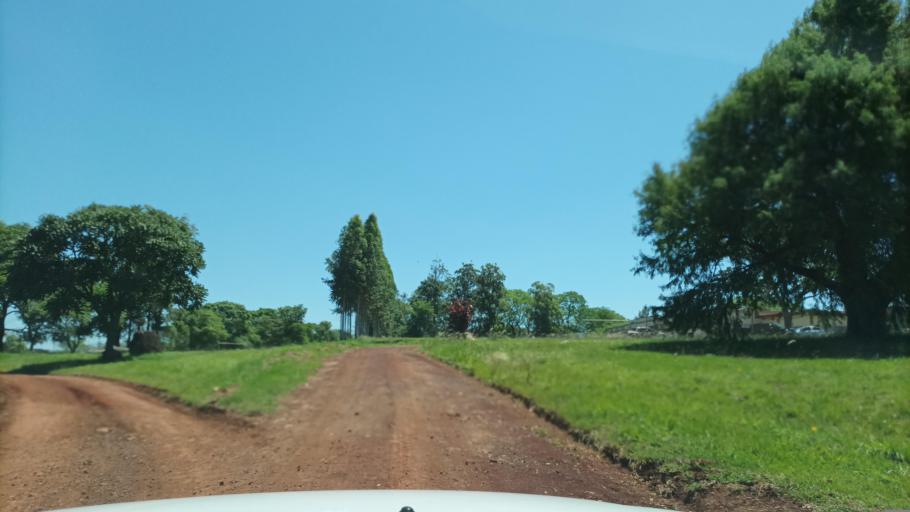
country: AR
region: Misiones
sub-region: Departamento de Apostoles
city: San Jose
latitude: -27.7918
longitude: -55.7142
